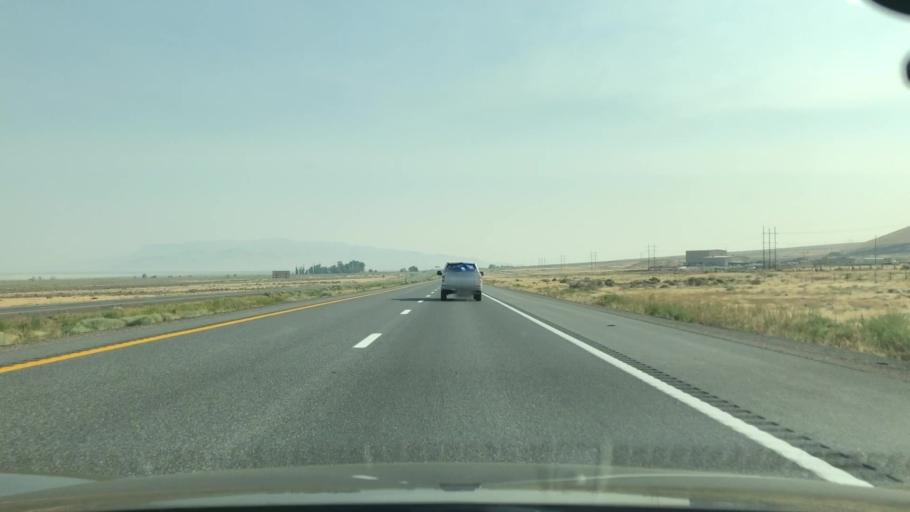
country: US
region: Nevada
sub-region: Pershing County
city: Lovelock
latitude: 40.5820
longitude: -118.2624
